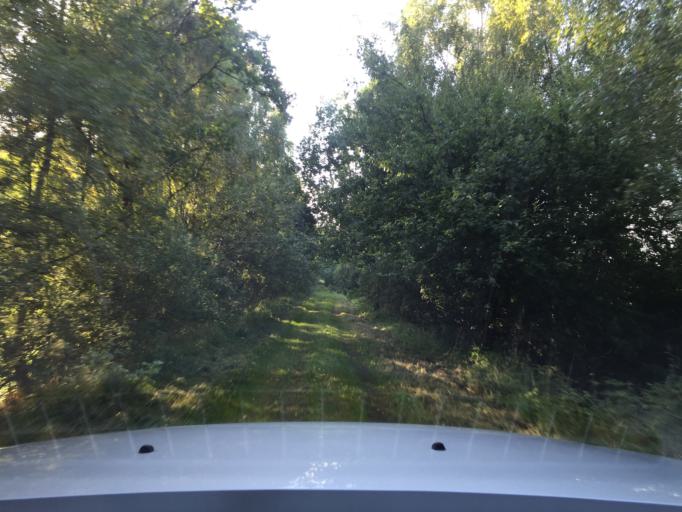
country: SE
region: Skane
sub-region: Hassleholms Kommun
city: Sosdala
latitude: 56.0173
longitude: 13.7178
